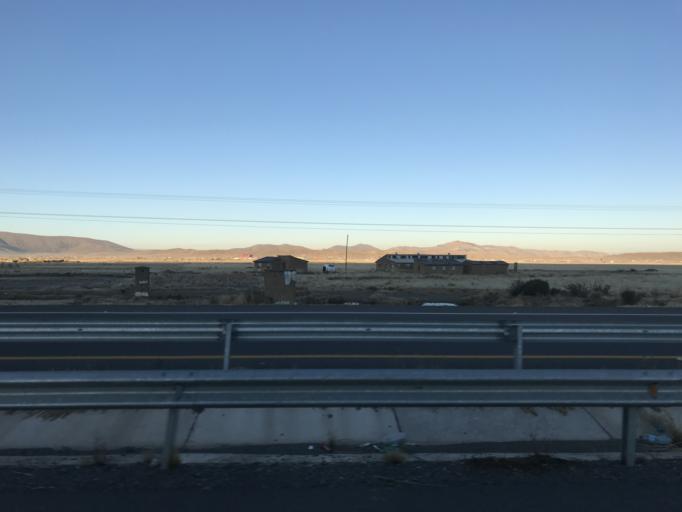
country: BO
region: La Paz
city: Batallas
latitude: -16.2890
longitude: -68.5422
